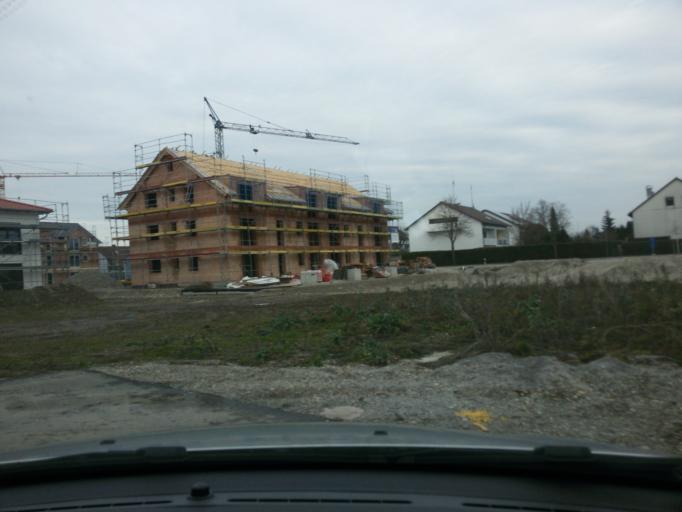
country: DE
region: Bavaria
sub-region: Swabia
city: Untermeitingen
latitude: 48.1682
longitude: 10.8086
